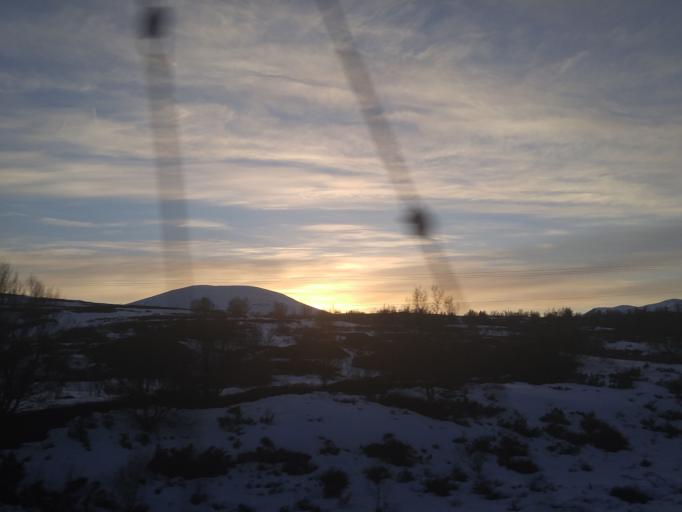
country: NO
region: Sor-Trondelag
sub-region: Oppdal
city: Oppdal
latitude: 62.2774
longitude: 9.5822
